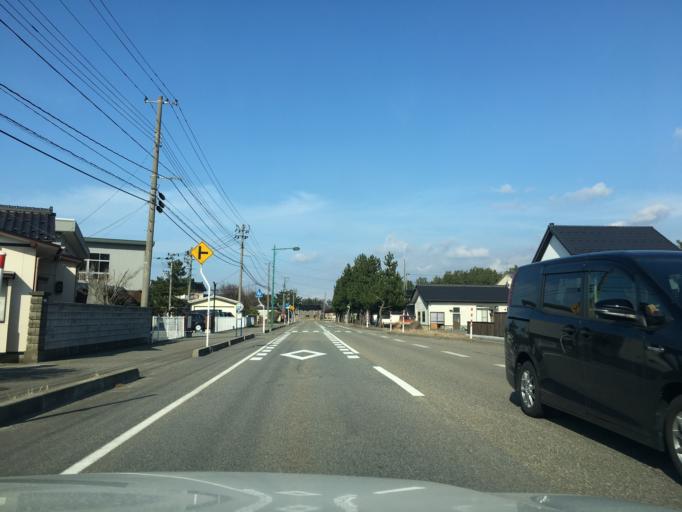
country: JP
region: Yamagata
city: Tsuruoka
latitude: 38.7899
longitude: 139.7671
